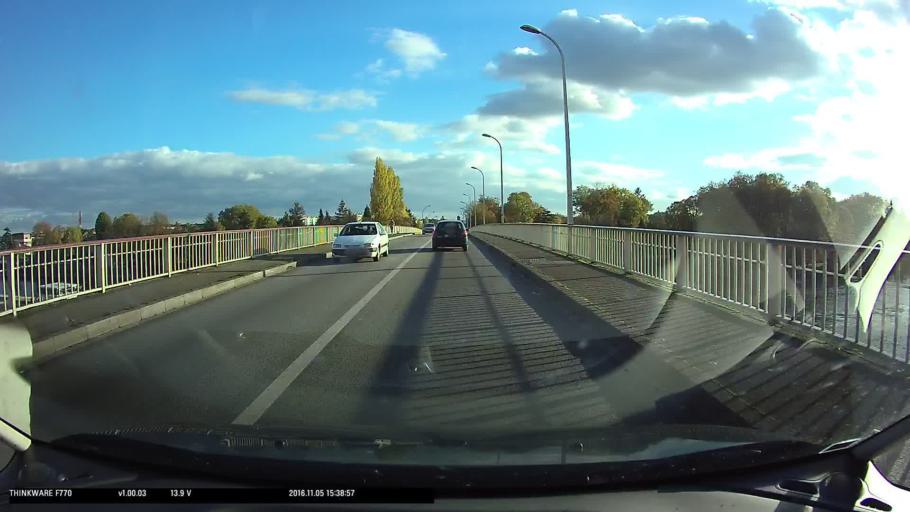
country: FR
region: Ile-de-France
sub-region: Departement des Yvelines
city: Meulan-en-Yvelines
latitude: 49.0004
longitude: 1.9072
